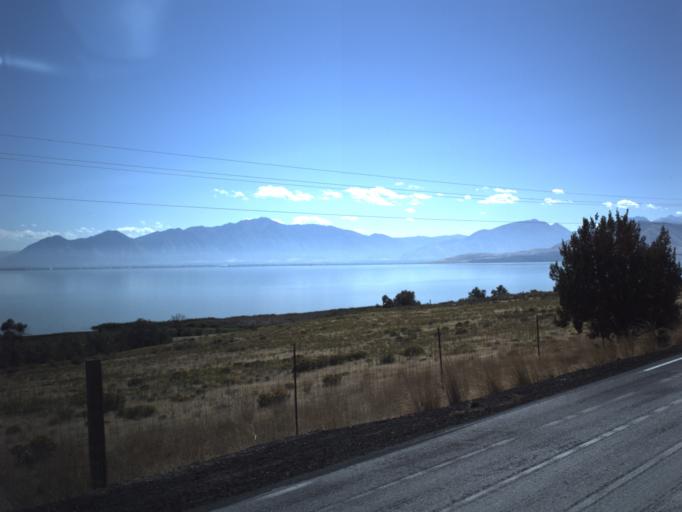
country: US
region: Utah
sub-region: Utah County
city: Saratoga Springs
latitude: 40.2415
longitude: -111.8668
